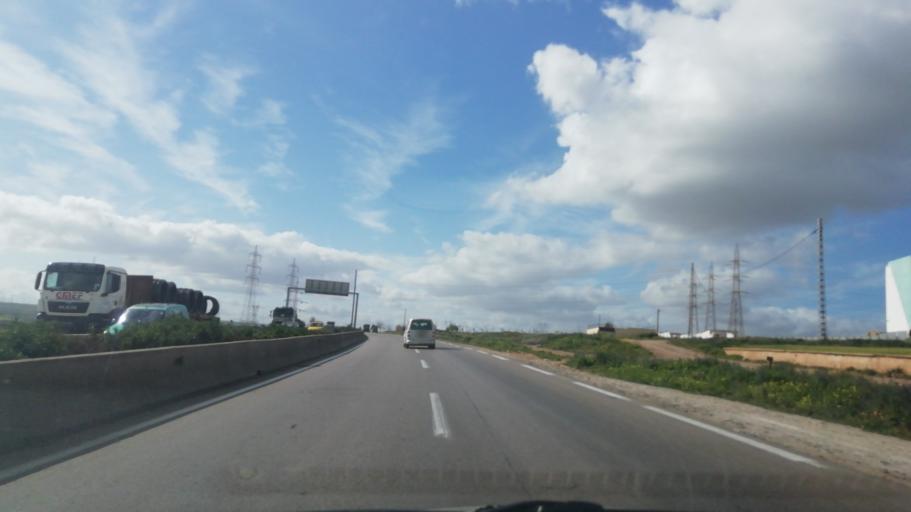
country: DZ
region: Oran
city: Ain el Bya
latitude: 35.7849
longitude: -0.1806
